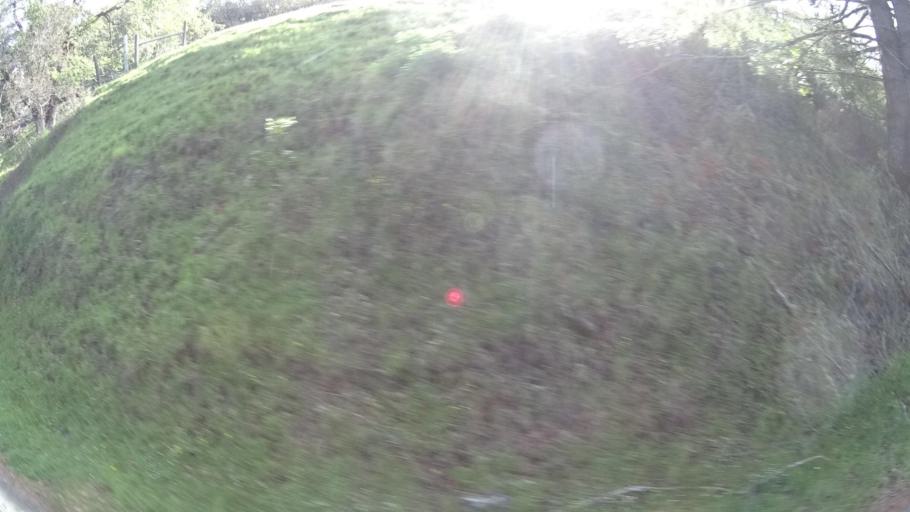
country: US
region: California
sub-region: Humboldt County
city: Hydesville
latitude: 40.6418
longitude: -123.9049
